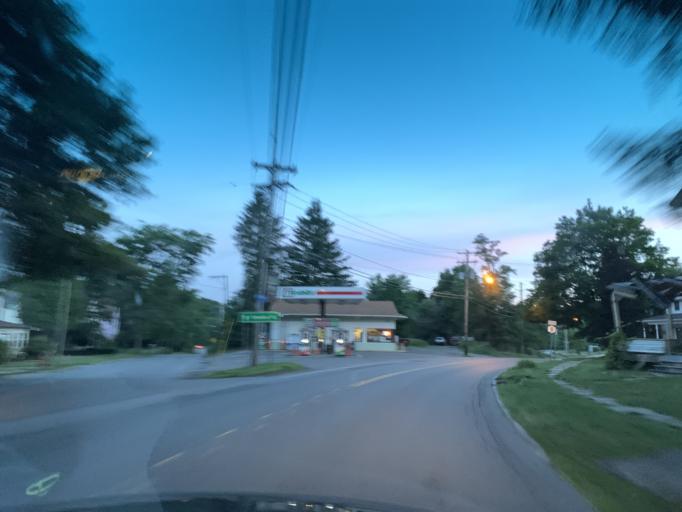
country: US
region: New York
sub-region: Chenango County
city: New Berlin
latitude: 42.6194
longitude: -75.3319
